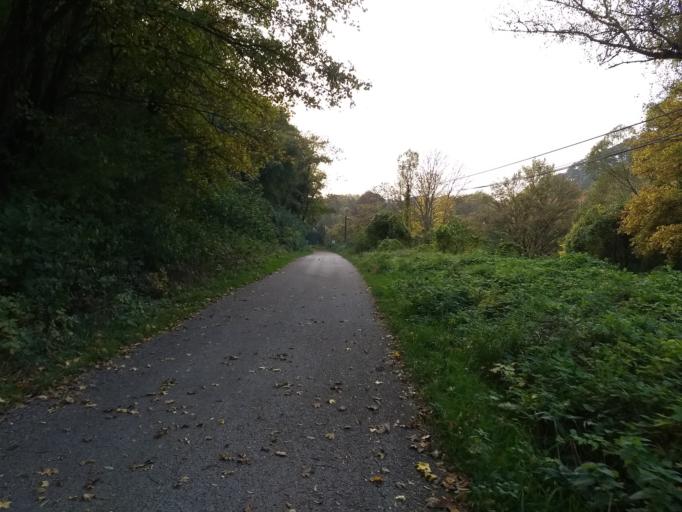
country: AT
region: Lower Austria
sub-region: Politischer Bezirk Modling
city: Perchtoldsdorf
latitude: 48.1310
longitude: 16.2466
